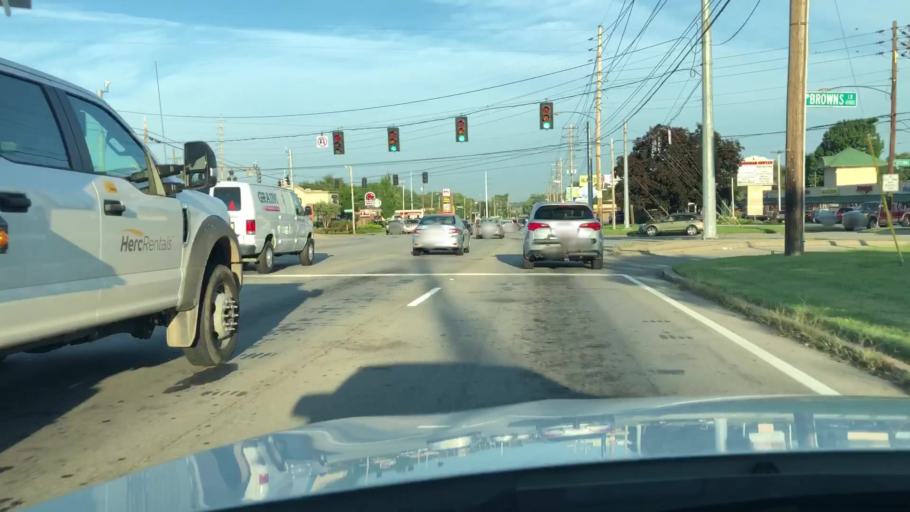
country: US
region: Kentucky
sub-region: Jefferson County
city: Saint Regis Park
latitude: 38.2199
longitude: -85.6250
